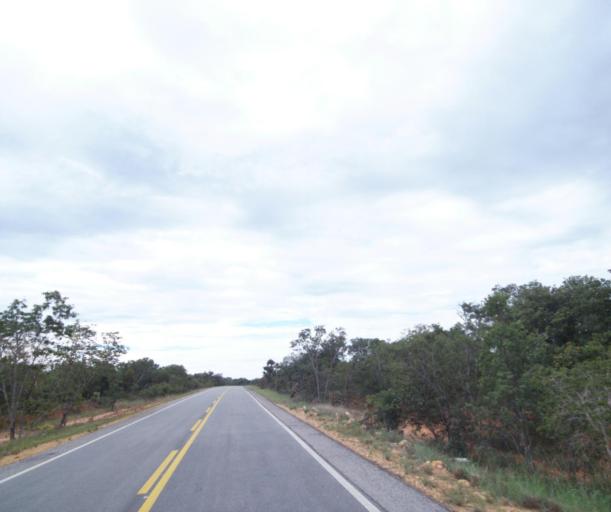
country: BR
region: Bahia
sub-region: Sao Felix Do Coribe
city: Santa Maria da Vitoria
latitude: -13.9501
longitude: -44.4457
